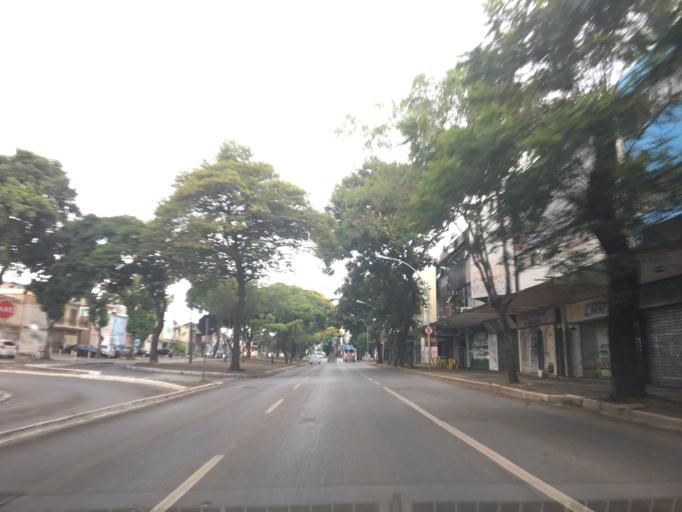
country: BR
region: Federal District
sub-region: Brasilia
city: Brasilia
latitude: -15.8111
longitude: -47.9045
